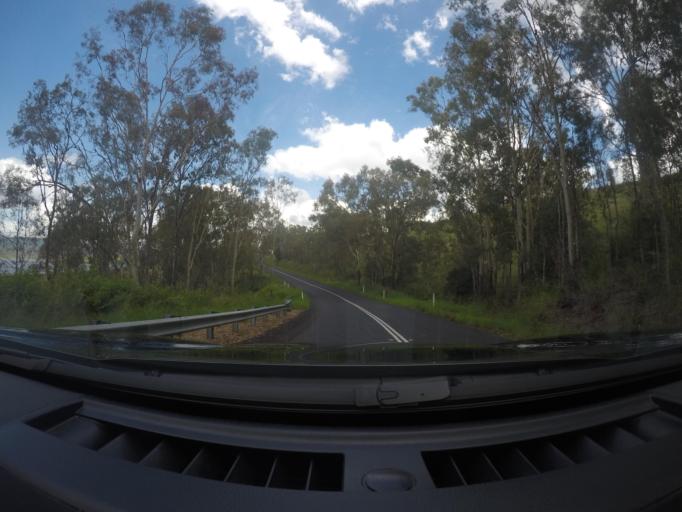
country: AU
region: Queensland
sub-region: Moreton Bay
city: Woodford
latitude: -27.0758
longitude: 152.5661
